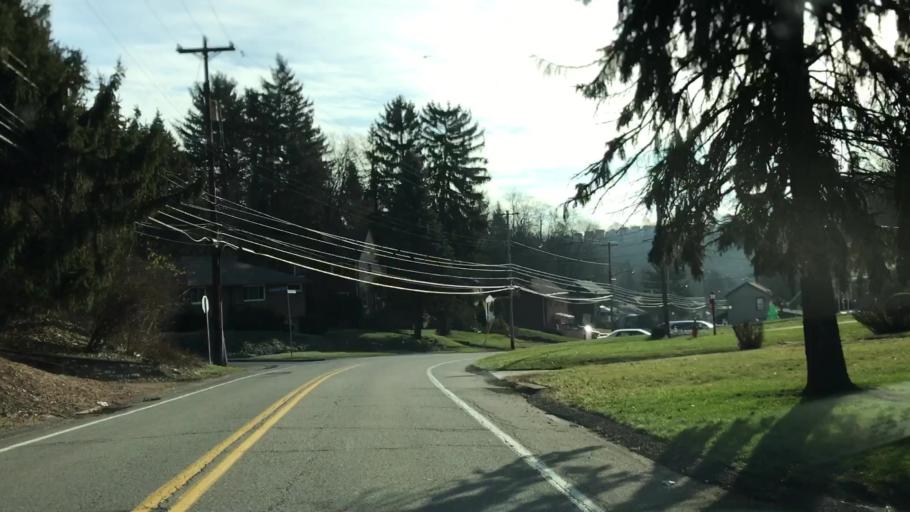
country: US
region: Pennsylvania
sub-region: Allegheny County
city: Green Tree
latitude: 40.4071
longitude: -80.0452
